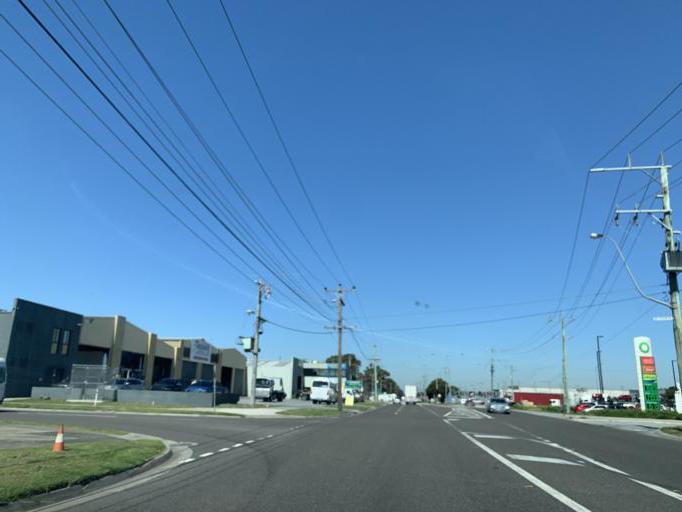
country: AU
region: Victoria
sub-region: Greater Dandenong
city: Dandenong
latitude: -38.0120
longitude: 145.2061
